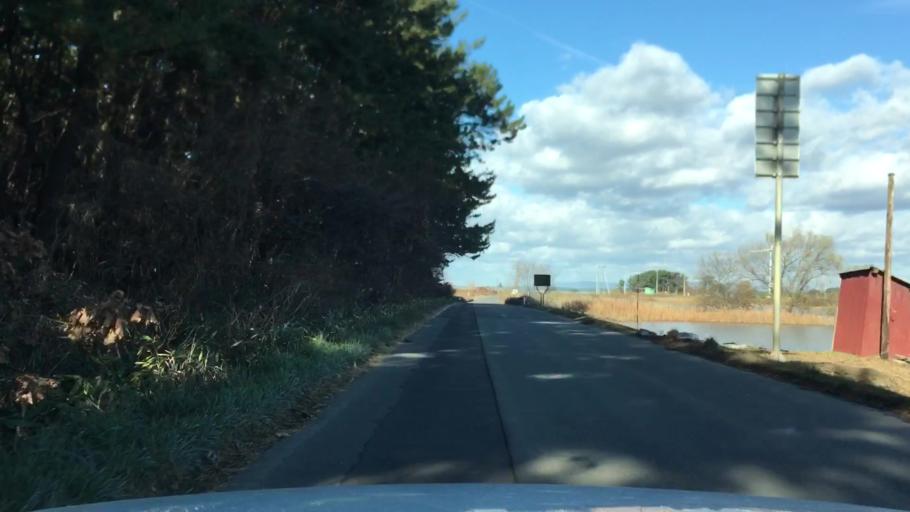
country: JP
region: Aomori
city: Shimokizukuri
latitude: 40.8503
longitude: 140.3000
